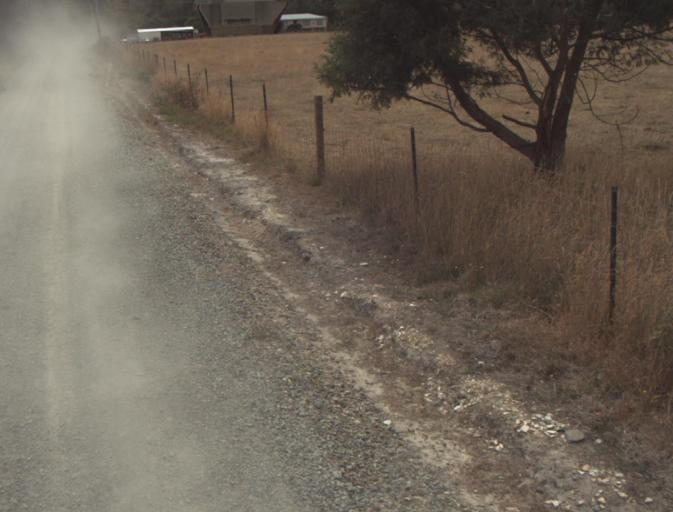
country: AU
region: Tasmania
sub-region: Launceston
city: Mayfield
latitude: -41.2403
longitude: 147.1619
